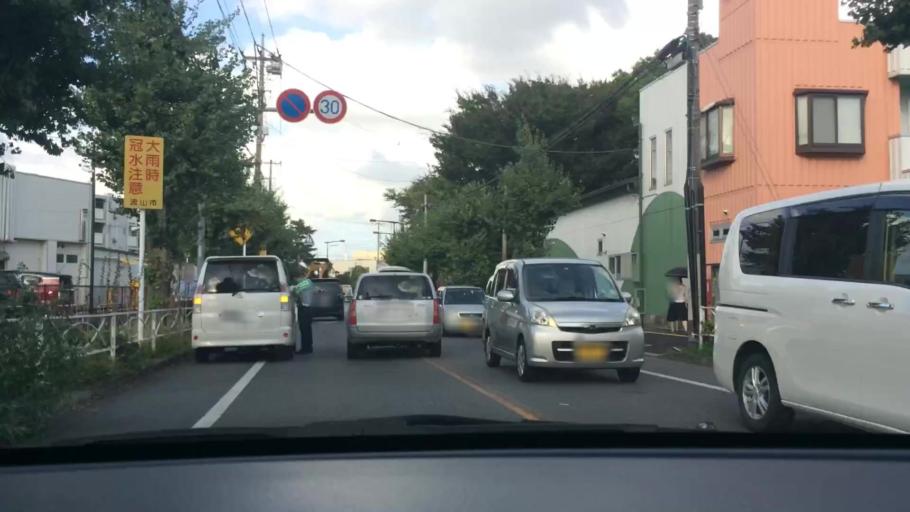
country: JP
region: Chiba
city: Nagareyama
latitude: 35.8987
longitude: 139.9125
